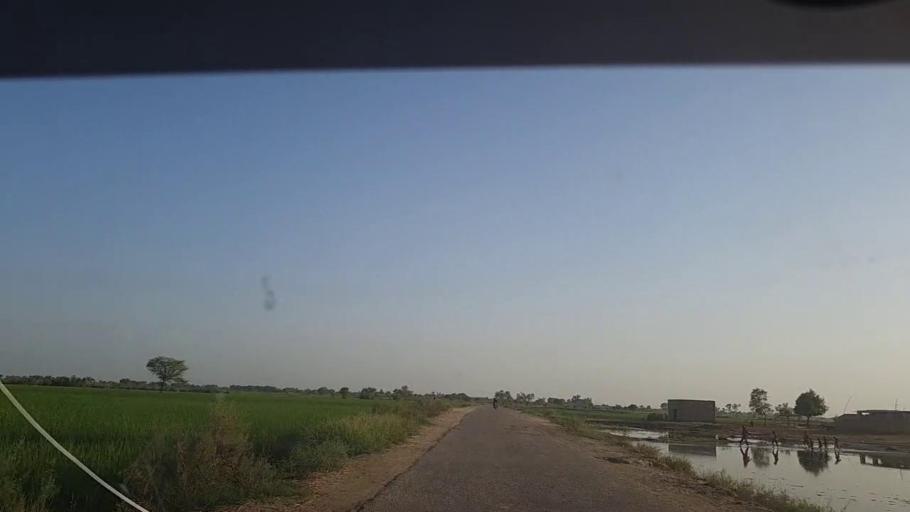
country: PK
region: Sindh
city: Thul
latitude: 28.1933
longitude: 68.8727
